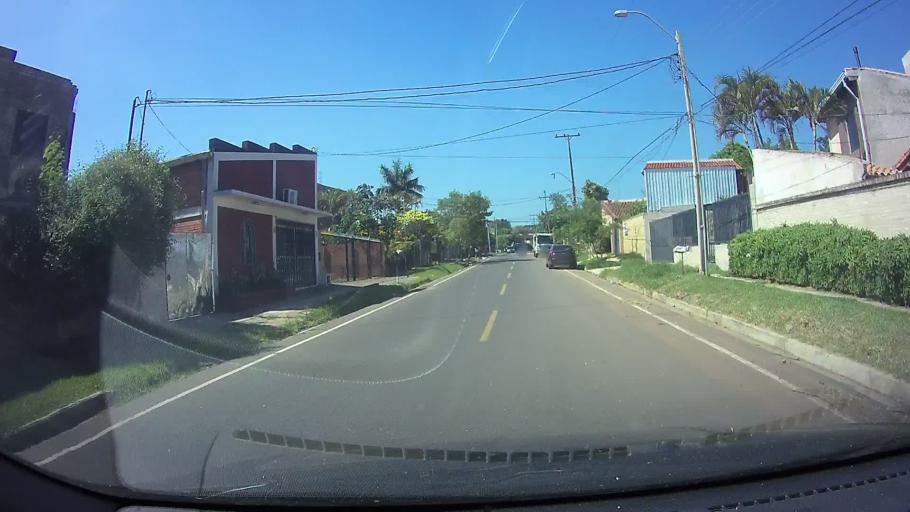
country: PY
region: Central
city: Fernando de la Mora
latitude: -25.2845
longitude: -57.5384
